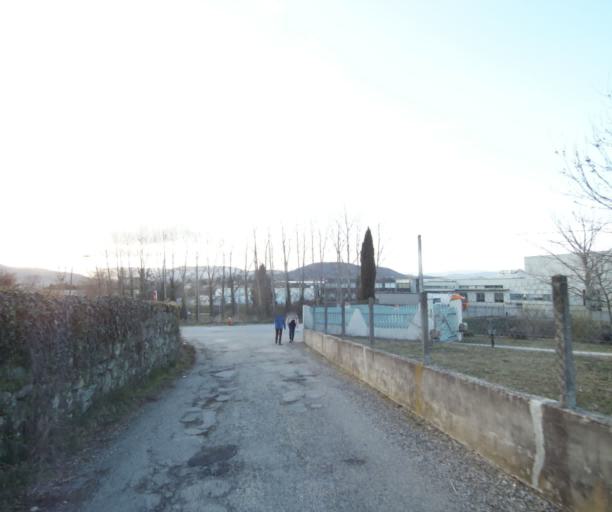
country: FR
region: Rhone-Alpes
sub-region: Departement de l'Ardeche
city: Annonay
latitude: 45.2423
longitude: 4.6924
